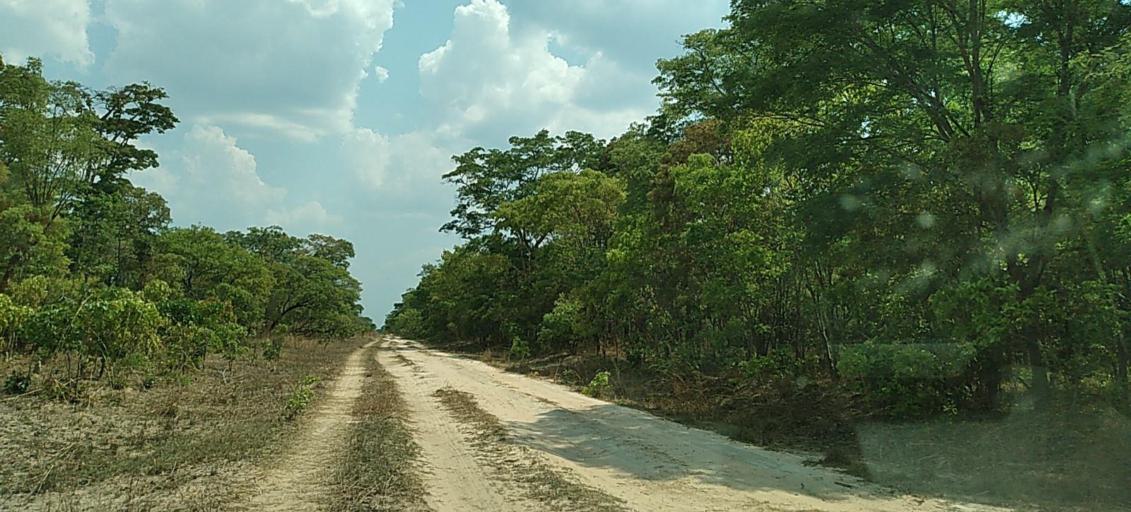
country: ZM
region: Copperbelt
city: Mpongwe
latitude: -13.8238
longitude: 27.9427
